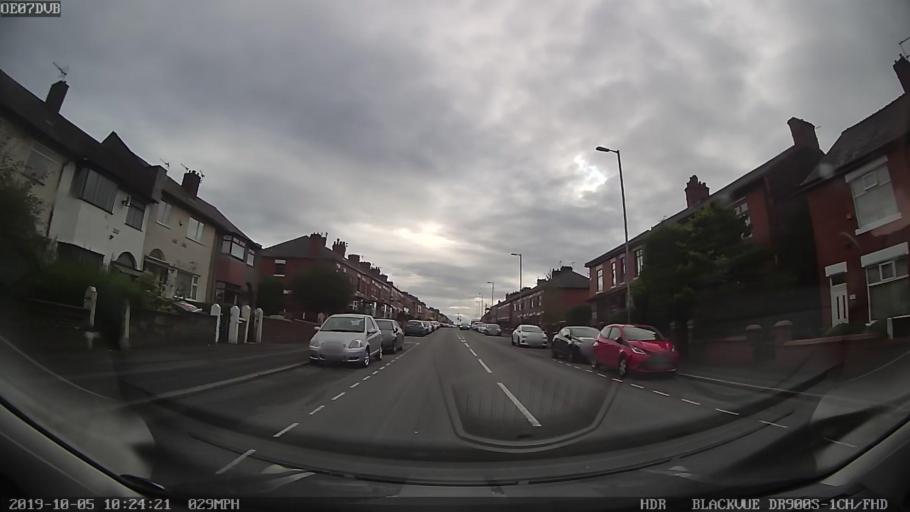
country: GB
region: England
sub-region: Borough of Rochdale
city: Middleton
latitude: 53.5513
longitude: -2.1676
